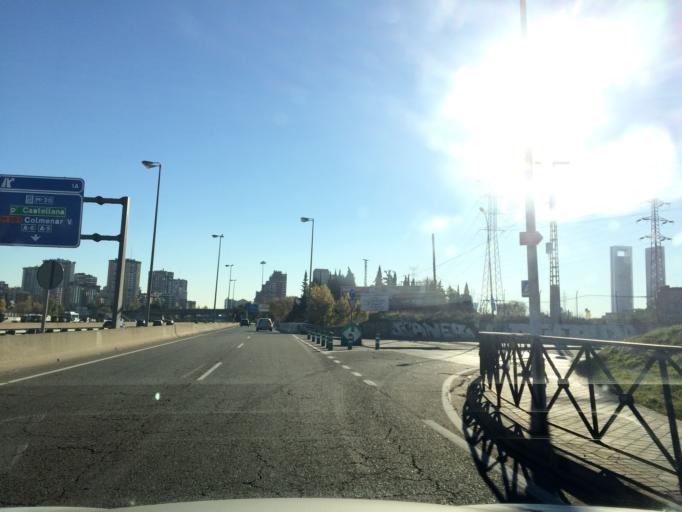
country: ES
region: Madrid
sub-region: Provincia de Madrid
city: Pinar de Chamartin
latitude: 40.4889
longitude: -3.6731
